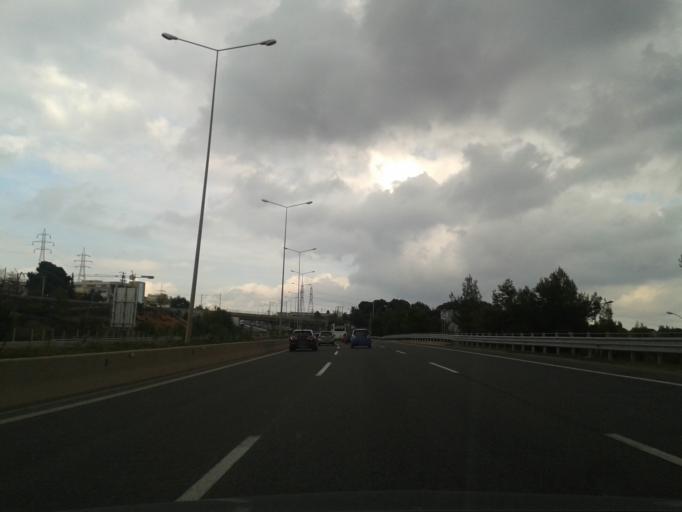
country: GR
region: Attica
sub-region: Nomarchia Athinas
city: Ekali
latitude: 38.1229
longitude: 23.8349
